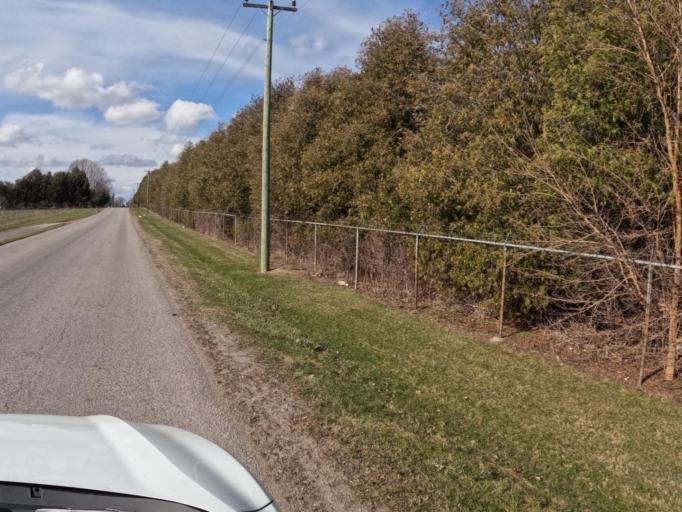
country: CA
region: Ontario
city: Norfolk County
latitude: 42.8589
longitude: -80.2733
